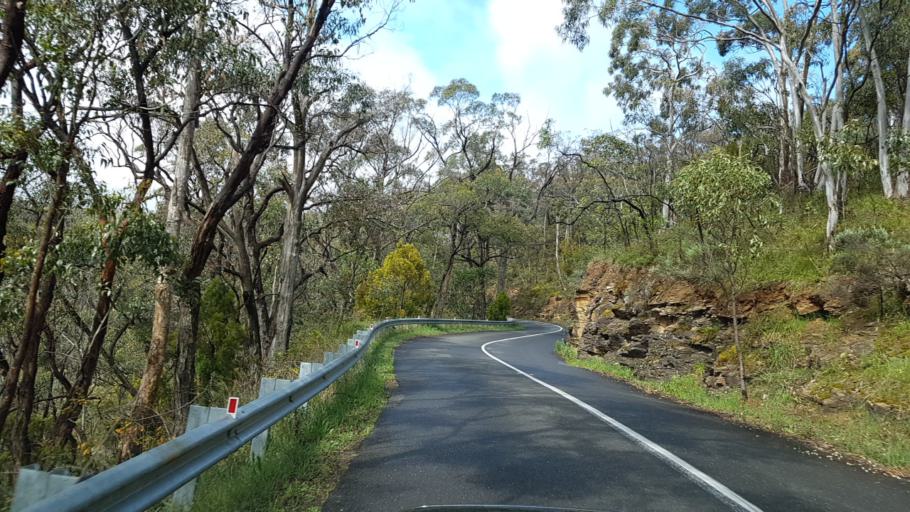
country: AU
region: South Australia
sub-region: Adelaide Hills
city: Adelaide Hills
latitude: -34.9120
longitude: 138.7572
